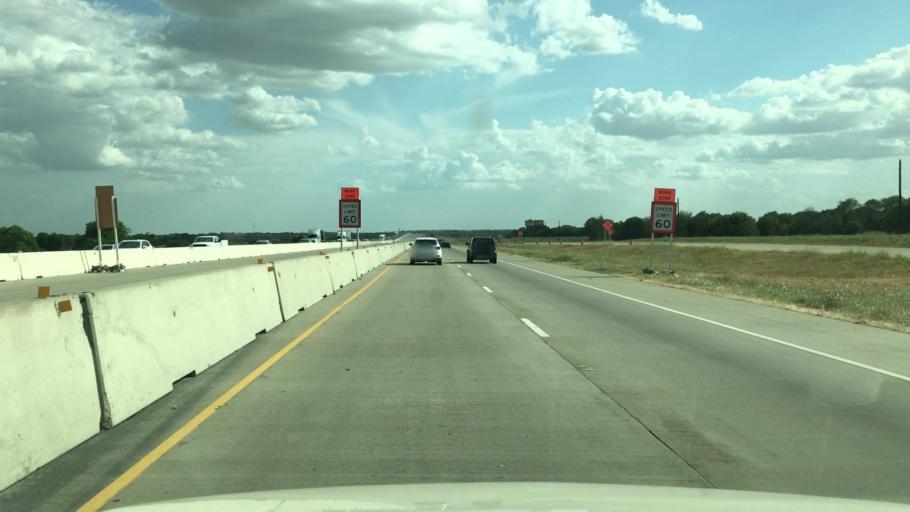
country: US
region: Texas
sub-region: Bell County
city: Troy
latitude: 31.2457
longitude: -97.2816
